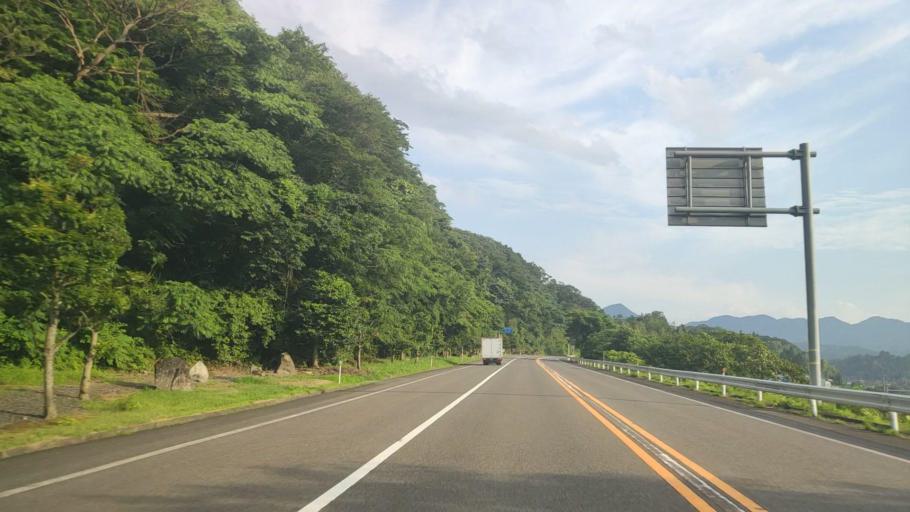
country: JP
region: Tottori
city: Kurayoshi
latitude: 35.3588
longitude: 133.7517
